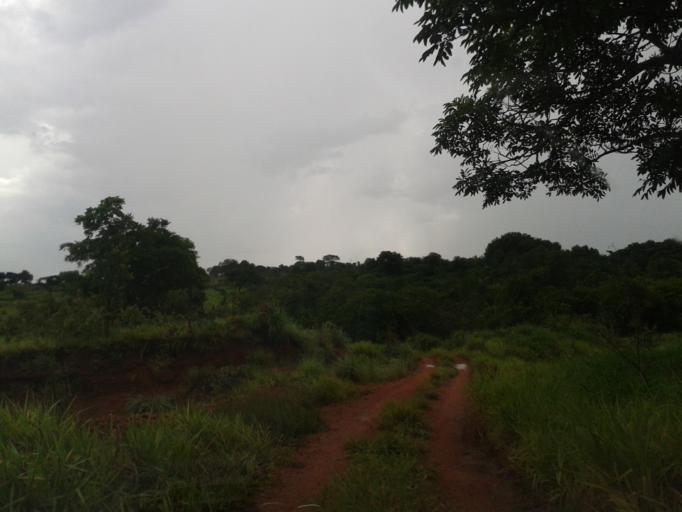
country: BR
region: Minas Gerais
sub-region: Santa Vitoria
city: Santa Vitoria
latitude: -19.1585
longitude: -50.5586
